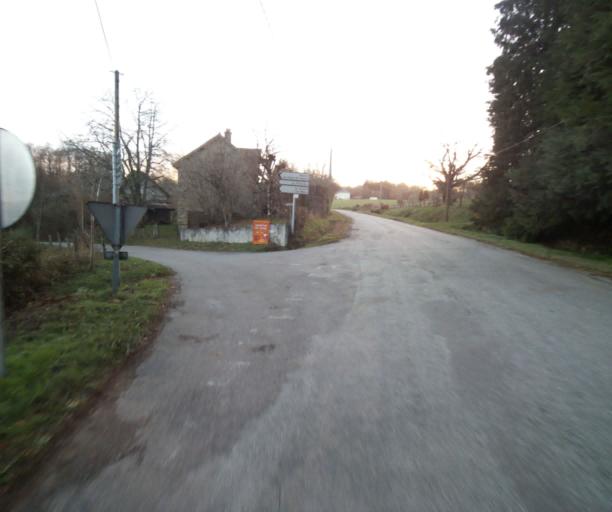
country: FR
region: Limousin
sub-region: Departement de la Correze
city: Laguenne
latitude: 45.2354
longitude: 1.7688
